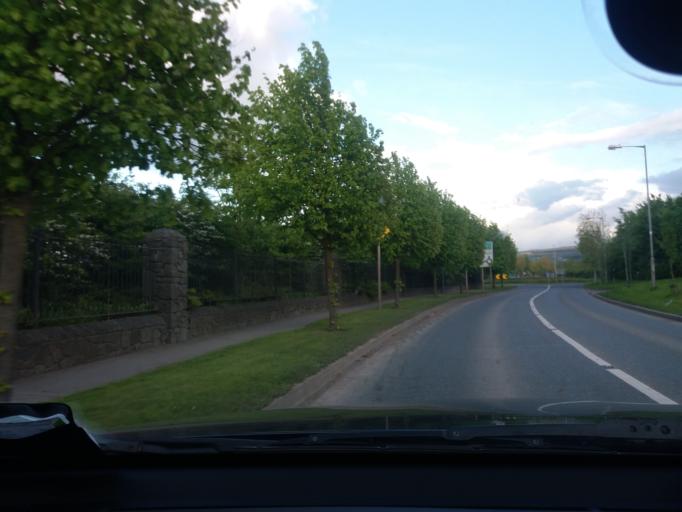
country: IE
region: Leinster
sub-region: South Dublin
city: Rathcoole
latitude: 53.2908
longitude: -6.4685
